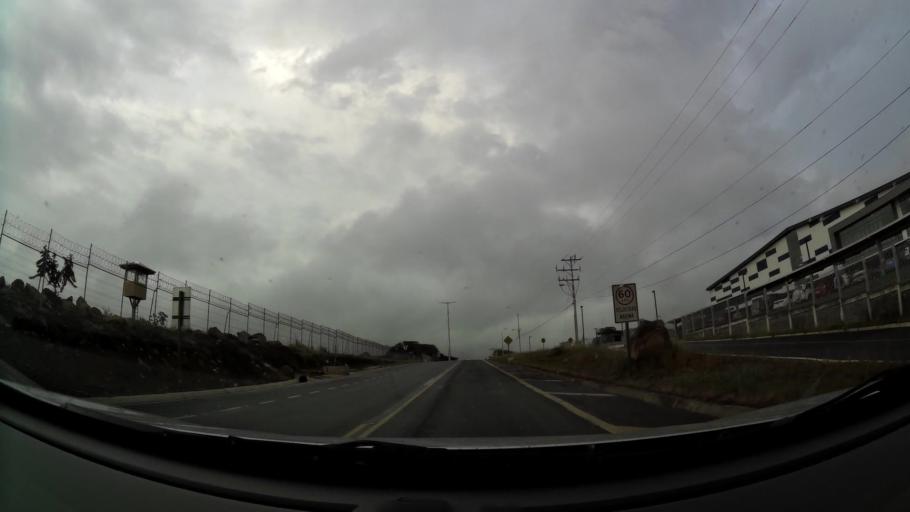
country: CR
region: Alajuela
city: Carrillos
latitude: 9.9748
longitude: -84.2763
